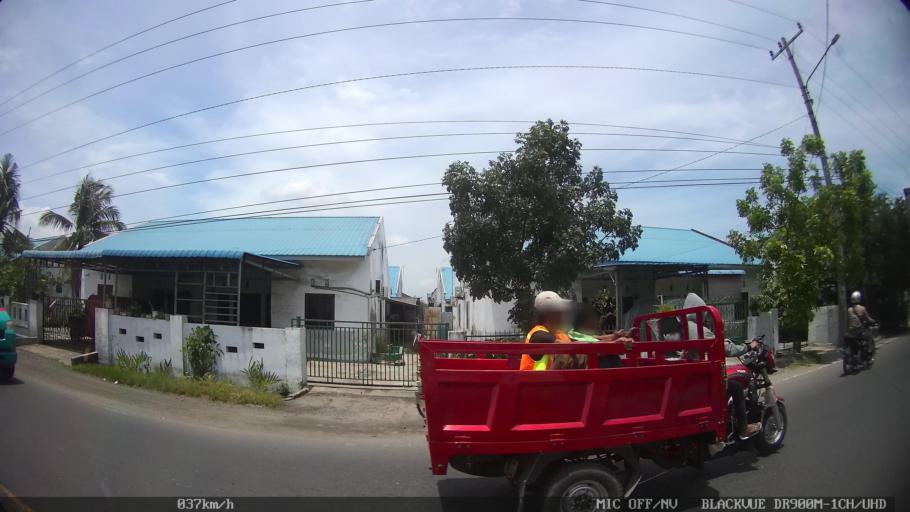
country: ID
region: North Sumatra
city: Belawan
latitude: 3.7675
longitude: 98.6826
